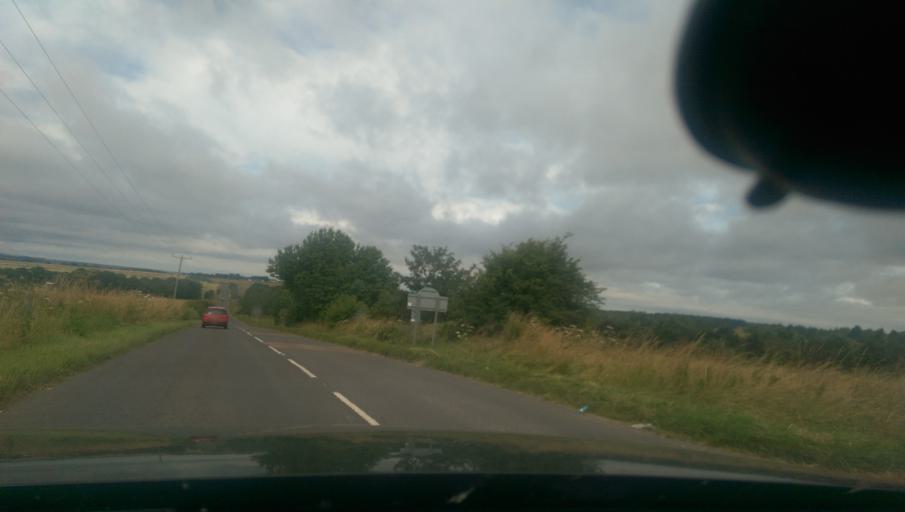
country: GB
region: England
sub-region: Wiltshire
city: Amesbury
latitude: 51.1986
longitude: -1.8255
